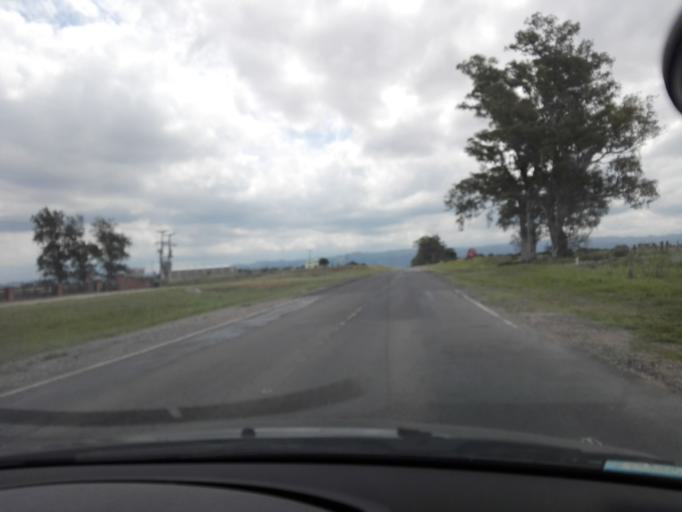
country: AR
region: Cordoba
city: Alta Gracia
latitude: -31.6581
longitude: -64.3756
